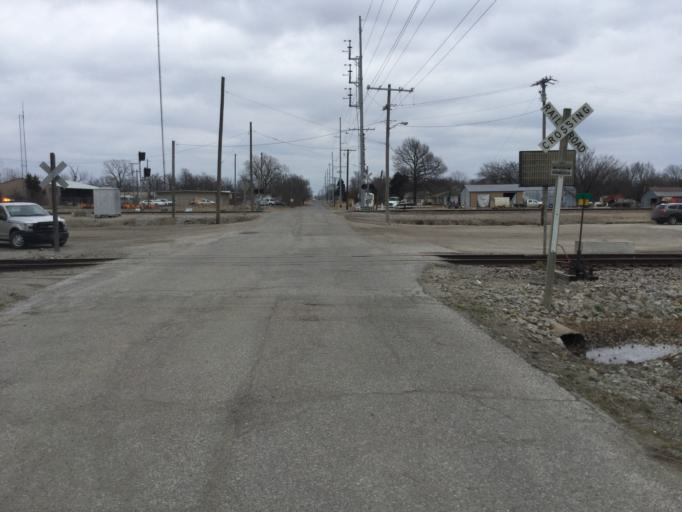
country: US
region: Kansas
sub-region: Cherokee County
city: Columbus
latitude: 37.1635
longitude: -94.8389
